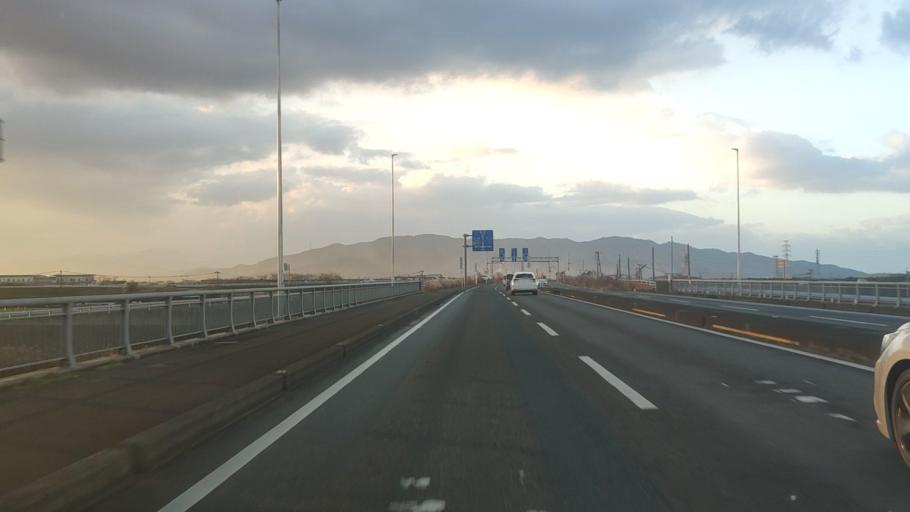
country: JP
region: Kumamoto
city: Kumamoto
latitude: 32.7403
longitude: 130.7047
